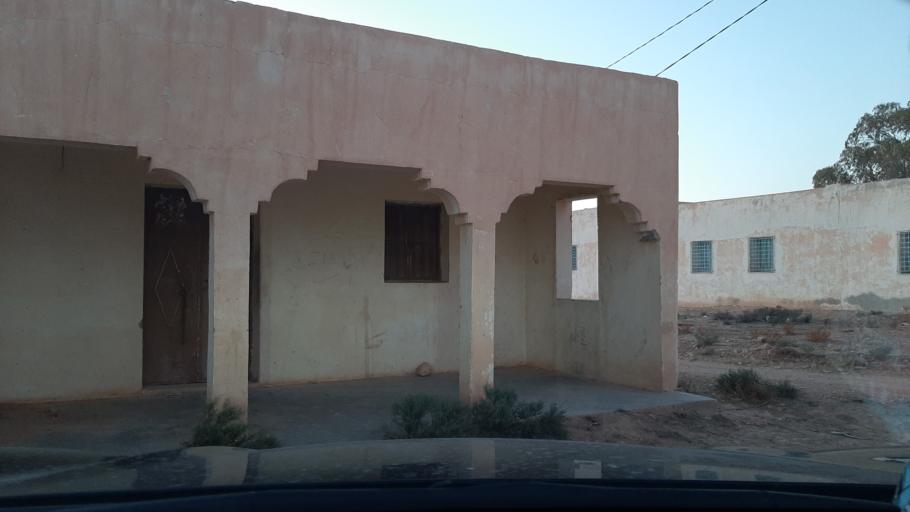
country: TN
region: Qabis
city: Matmata
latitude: 33.5709
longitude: 10.1788
